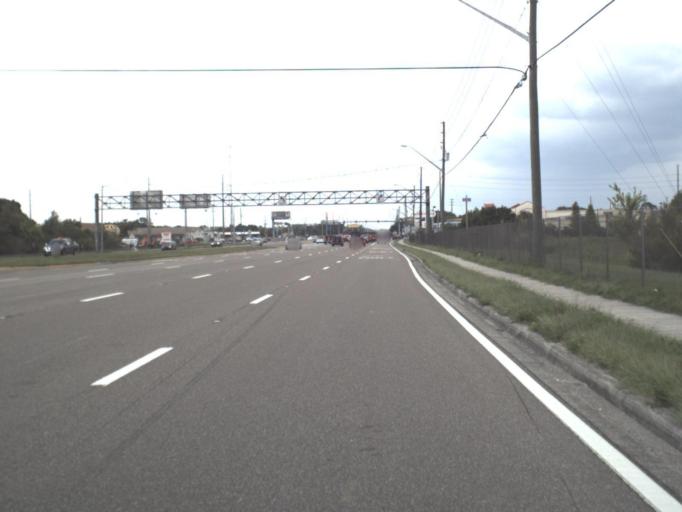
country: US
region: Florida
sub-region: Pasco County
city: Land O' Lakes
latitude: 28.1886
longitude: -82.4662
